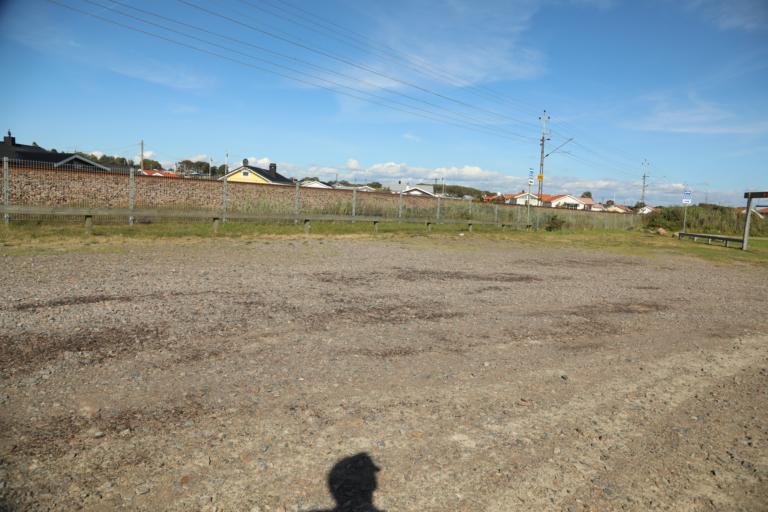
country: SE
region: Halland
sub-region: Varbergs Kommun
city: Varberg
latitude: 57.0828
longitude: 12.2618
